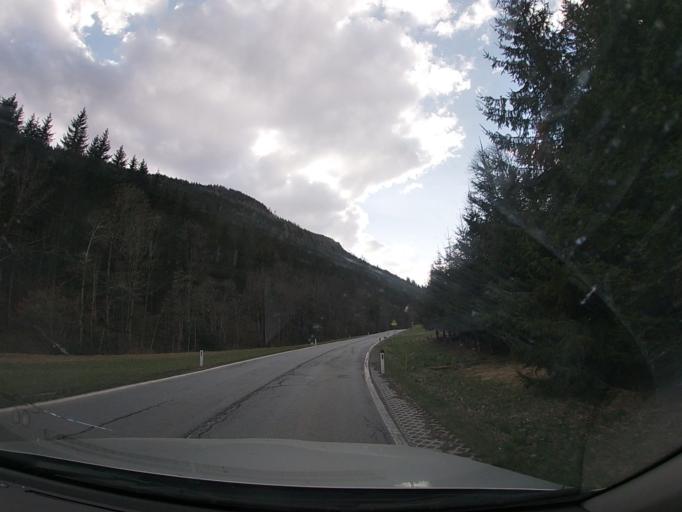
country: AT
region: Styria
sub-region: Politischer Bezirk Murau
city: Murau
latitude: 47.1391
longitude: 14.1438
